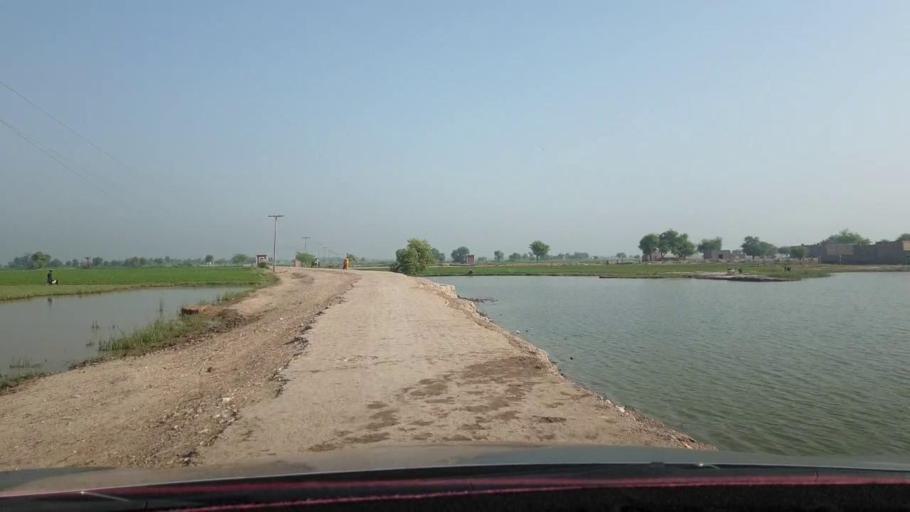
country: PK
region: Sindh
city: Nasirabad
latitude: 27.4255
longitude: 67.9222
